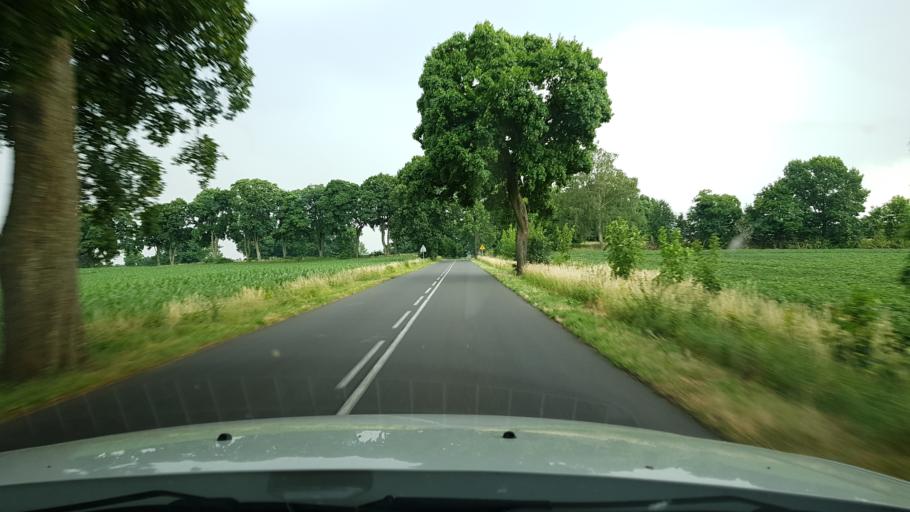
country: PL
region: West Pomeranian Voivodeship
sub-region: Powiat lobeski
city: Lobez
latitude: 53.6805
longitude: 15.6770
